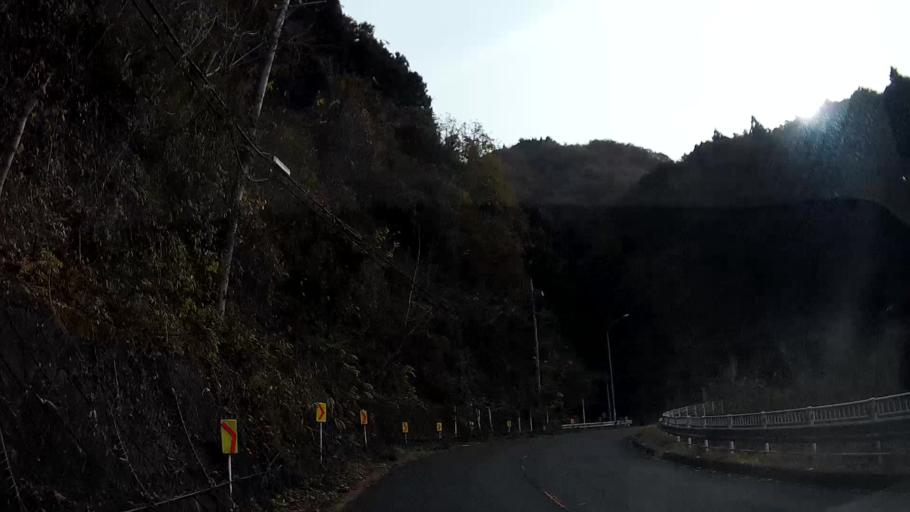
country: JP
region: Saitama
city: Chichibu
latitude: 35.9564
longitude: 139.0561
